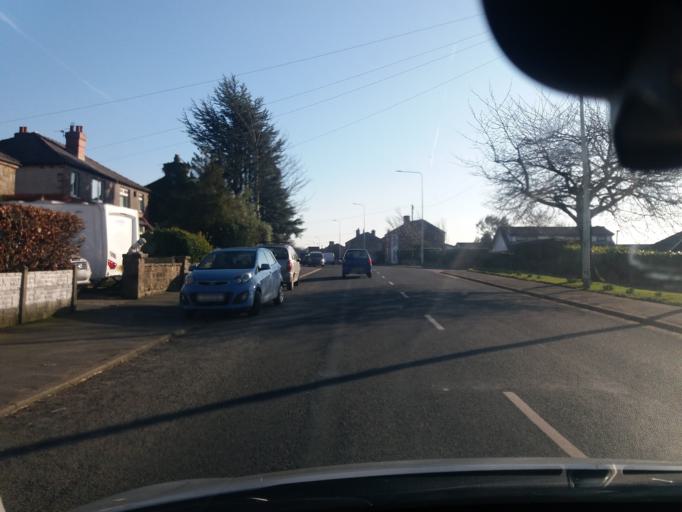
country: GB
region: England
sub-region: Lancashire
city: Adlington
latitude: 53.6247
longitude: -2.6072
